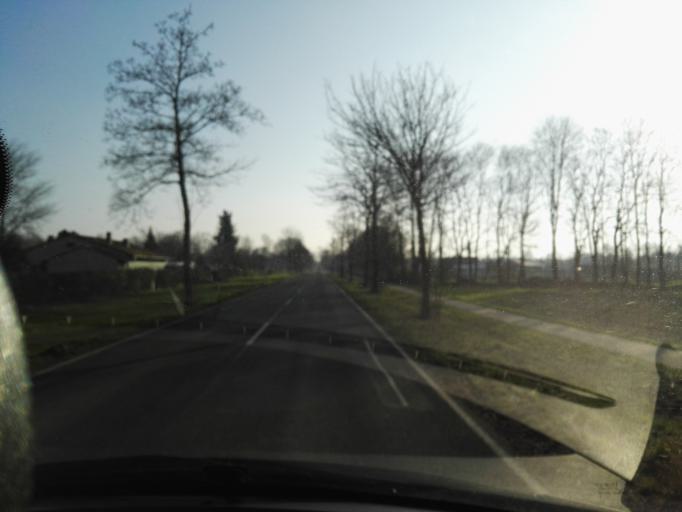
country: DE
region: Lower Saxony
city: Sarstedt
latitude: 52.2415
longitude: 9.8415
